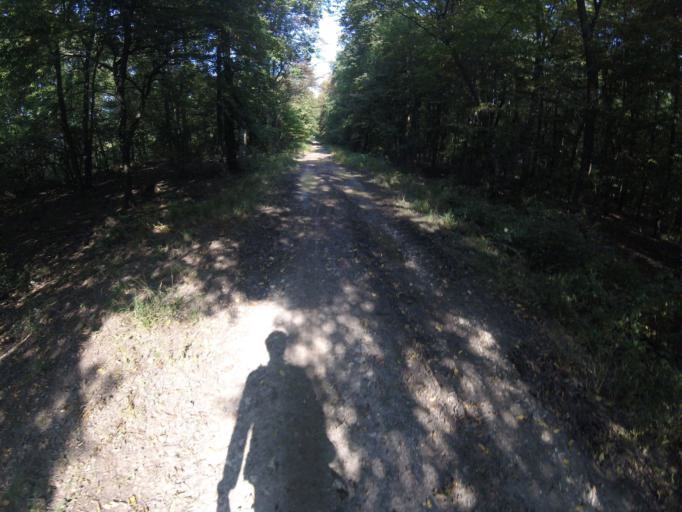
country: HU
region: Komarom-Esztergom
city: Kesztolc
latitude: 47.7634
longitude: 18.8129
